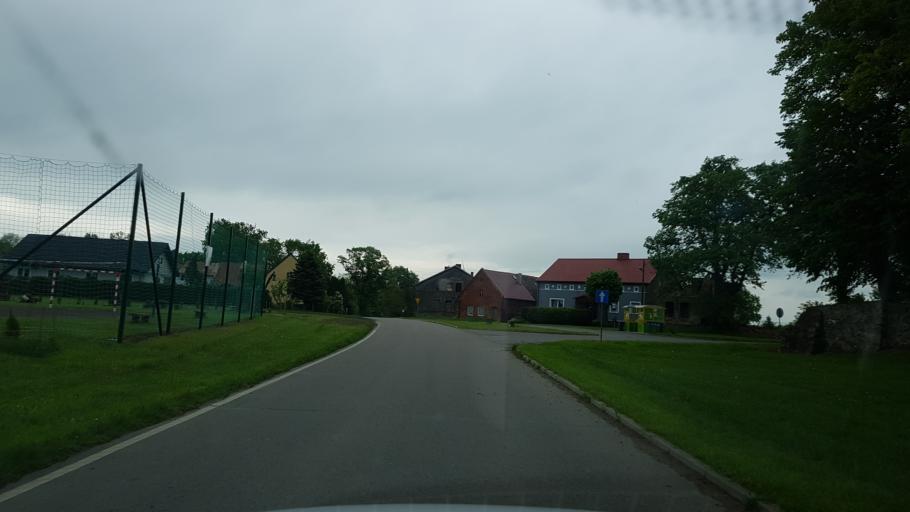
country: PL
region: West Pomeranian Voivodeship
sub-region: Powiat pyrzycki
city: Bielice
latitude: 53.1343
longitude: 14.7495
